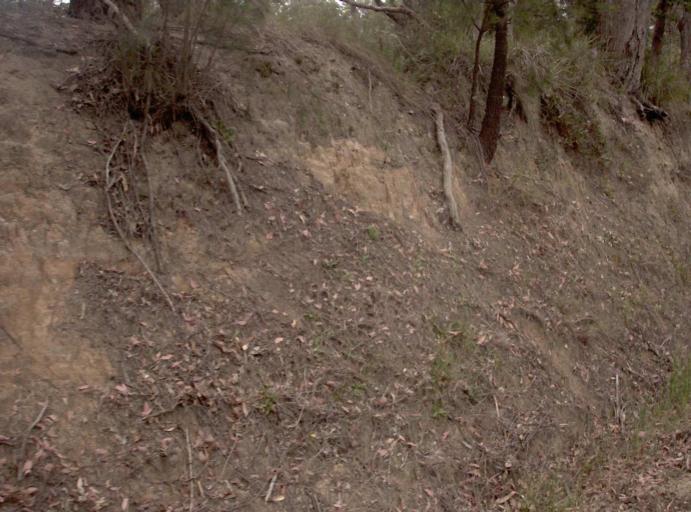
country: AU
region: Victoria
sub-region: East Gippsland
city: Bairnsdale
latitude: -37.7722
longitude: 147.5975
